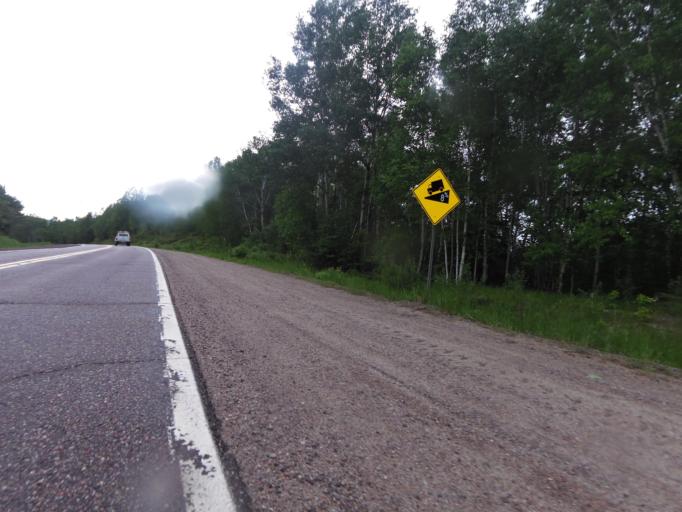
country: CA
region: Quebec
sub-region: Outaouais
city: Shawville
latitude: 45.9071
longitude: -76.2798
